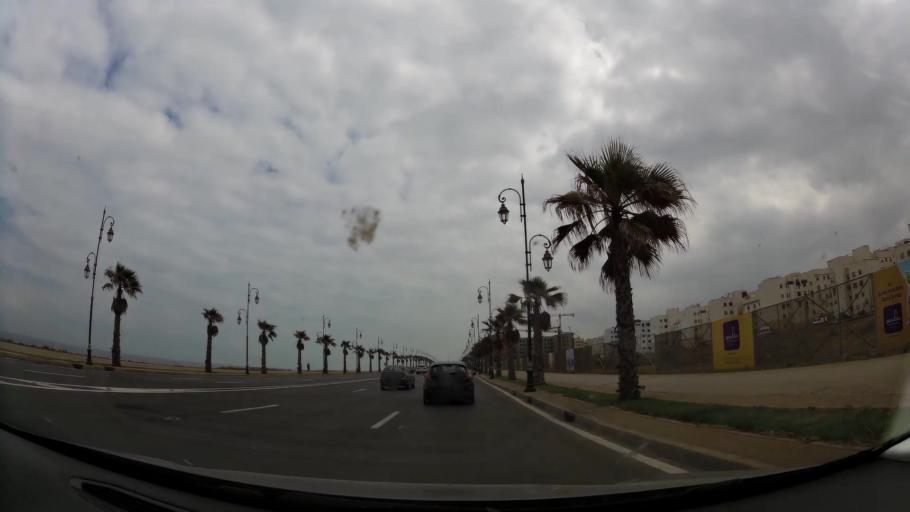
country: MA
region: Rabat-Sale-Zemmour-Zaer
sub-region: Rabat
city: Rabat
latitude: 33.9984
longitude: -6.8769
